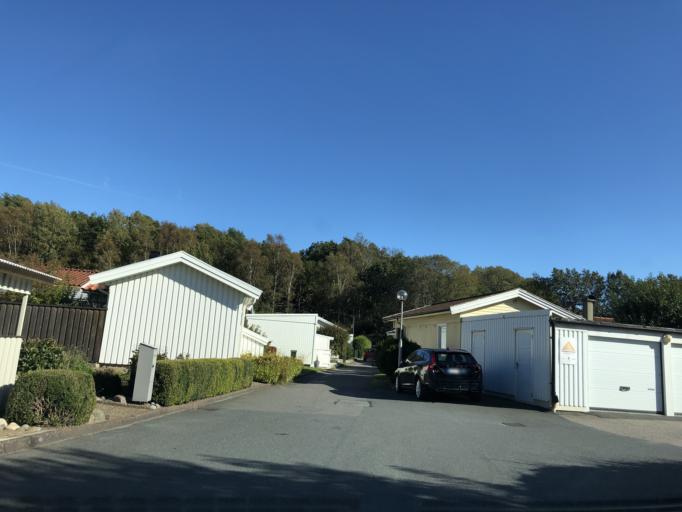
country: SE
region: Vaestra Goetaland
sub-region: Goteborg
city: Majorna
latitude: 57.6598
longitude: 11.8796
